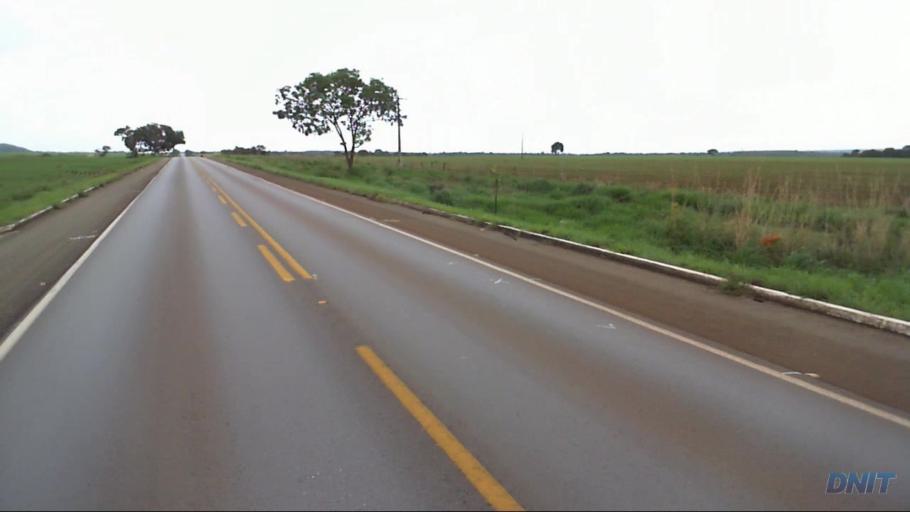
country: BR
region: Goias
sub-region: Barro Alto
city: Barro Alto
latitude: -14.8162
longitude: -49.0415
